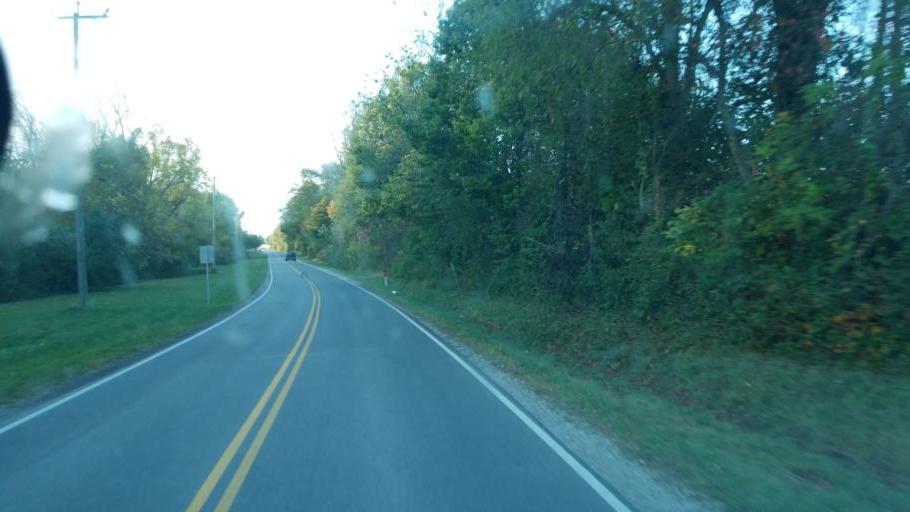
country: US
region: Ohio
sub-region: Licking County
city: Pataskala
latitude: 40.0192
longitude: -82.7282
